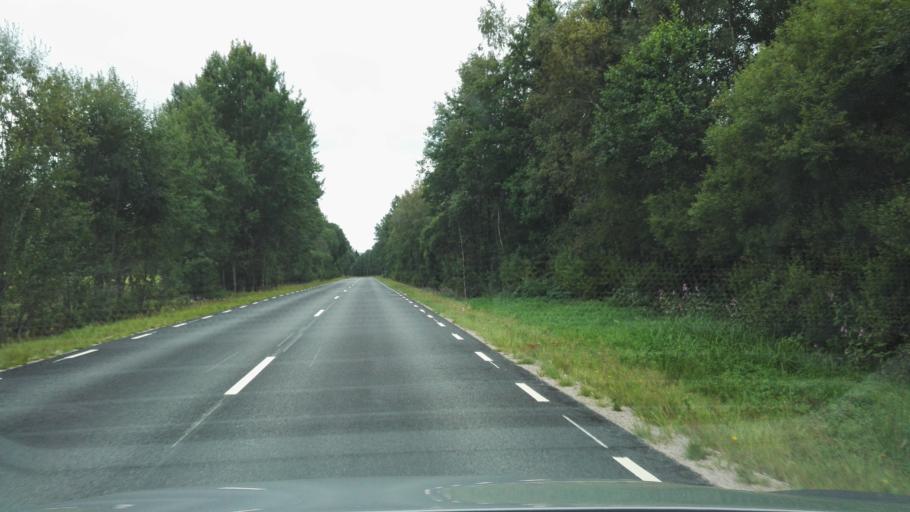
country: SE
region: Kronoberg
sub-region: Vaxjo Kommun
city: Braas
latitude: 57.1642
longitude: 14.9605
